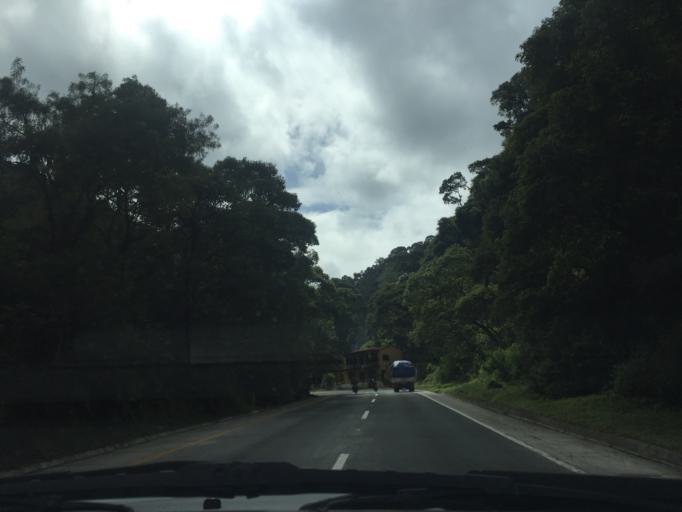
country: GT
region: Sacatepequez
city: Santa Lucia Milpas Altas
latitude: 14.5603
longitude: -90.6924
